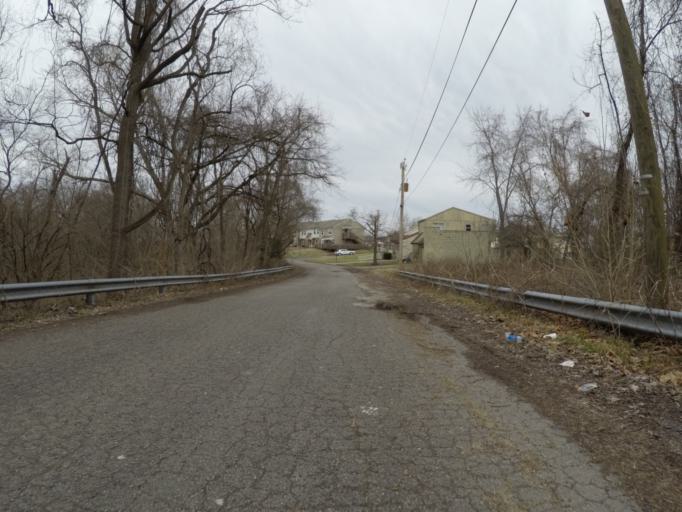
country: US
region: Ohio
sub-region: Lawrence County
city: Burlington
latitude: 38.4055
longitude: -82.4940
